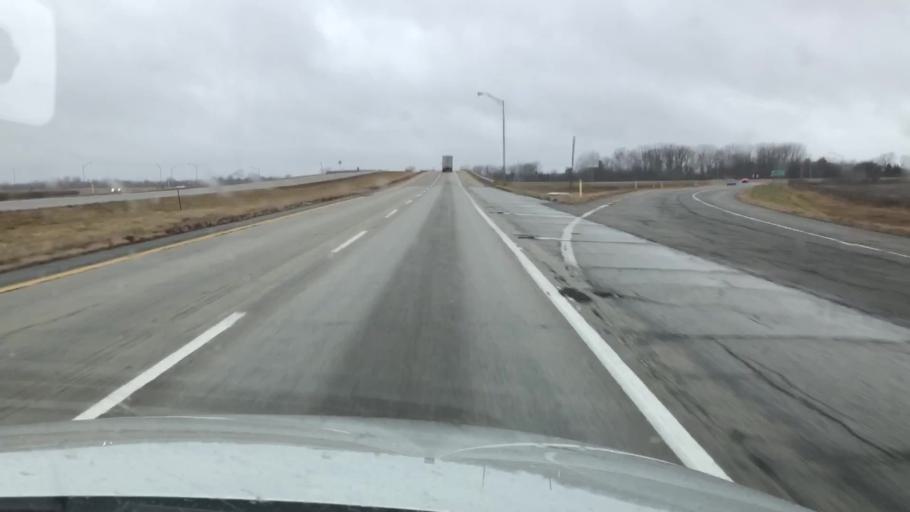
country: US
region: Indiana
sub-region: Starke County
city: Knox
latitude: 41.3940
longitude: -86.6161
